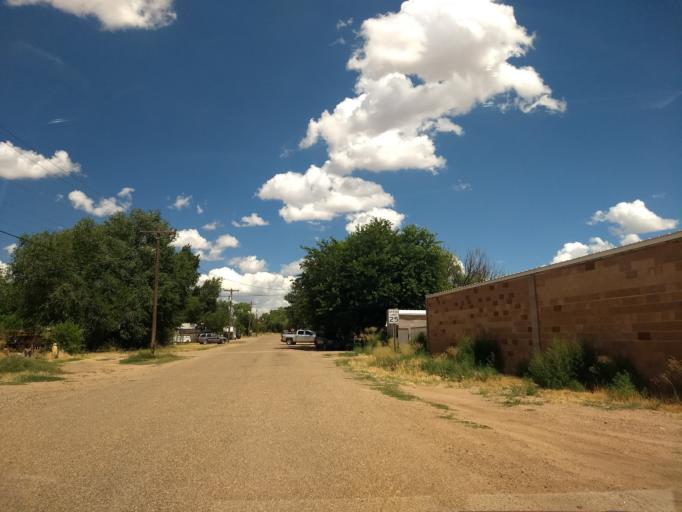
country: US
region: Arizona
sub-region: Coconino County
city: Fredonia
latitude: 36.9460
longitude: -112.5306
